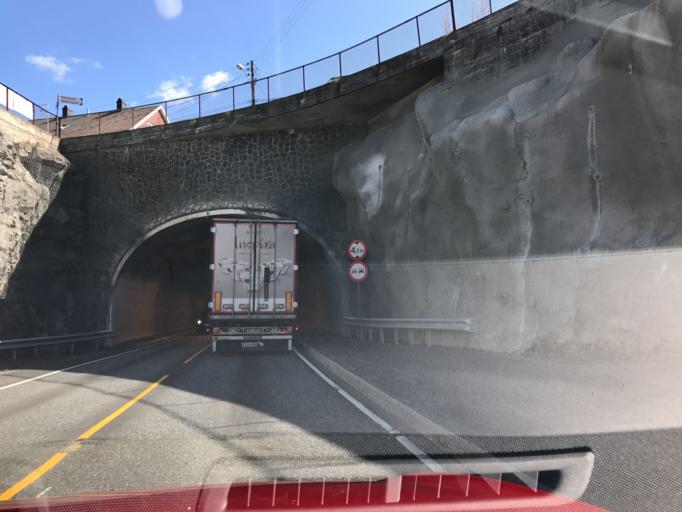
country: NO
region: Telemark
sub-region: Bamble
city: Langesund
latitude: 59.0555
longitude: 9.6926
